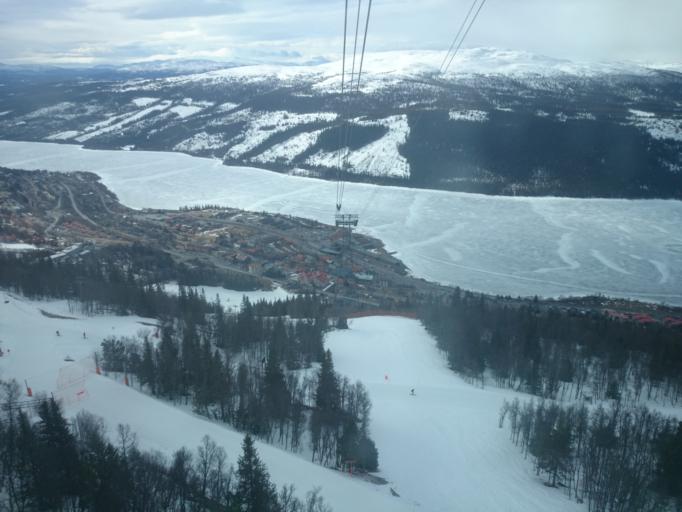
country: SE
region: Jaemtland
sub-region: Are Kommun
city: Are
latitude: 63.4095
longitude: 13.0776
